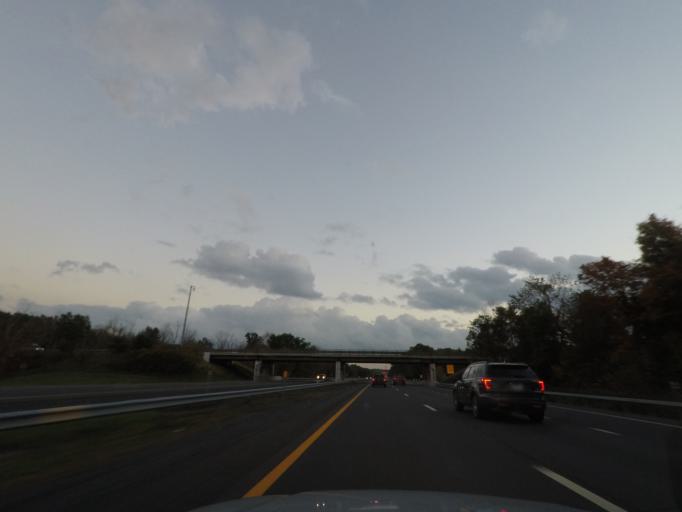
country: US
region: New York
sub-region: Ulster County
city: New Paltz
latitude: 41.7368
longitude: -74.0656
